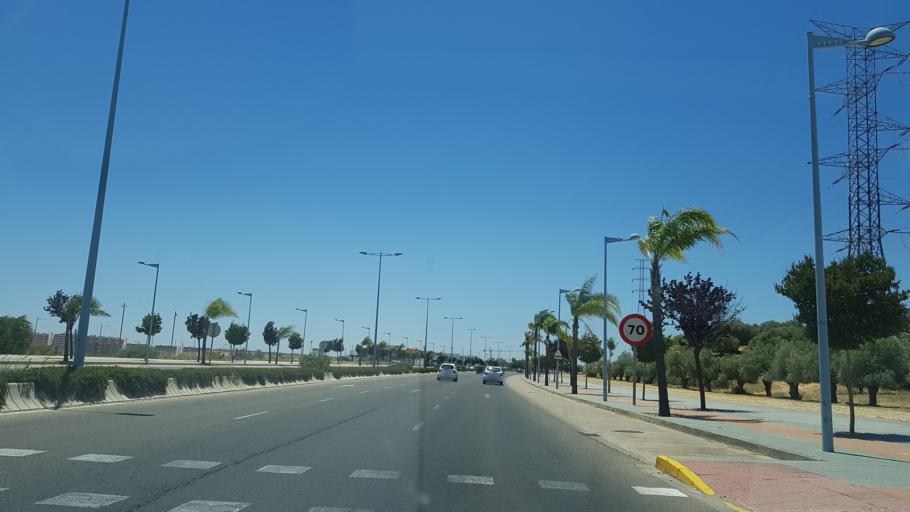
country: ES
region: Andalusia
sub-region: Provincia de Sevilla
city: Dos Hermanas
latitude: 37.3151
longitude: -5.9411
